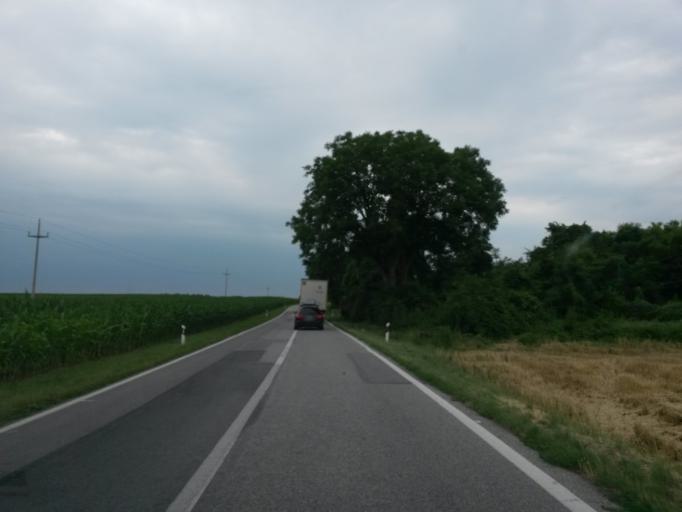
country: HR
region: Vukovarsko-Srijemska
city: Lovas
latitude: 45.2841
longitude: 19.1248
